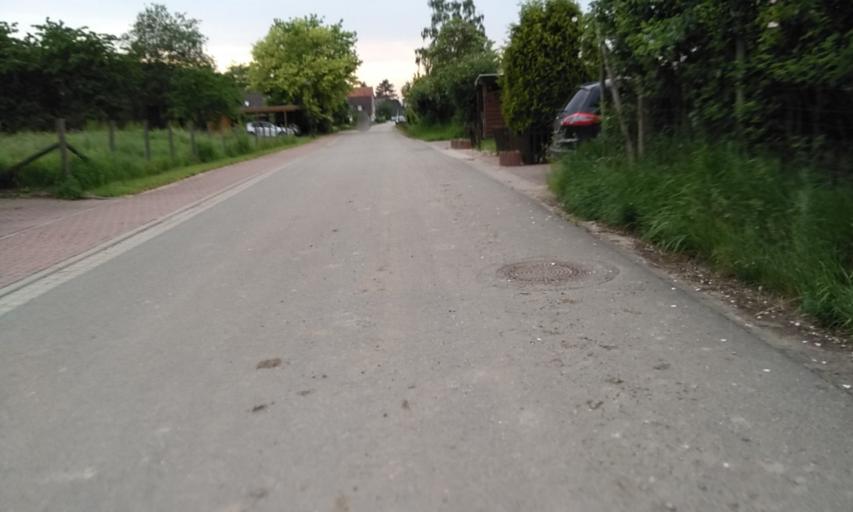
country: DE
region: Lower Saxony
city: Jork
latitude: 53.5127
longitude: 9.6952
